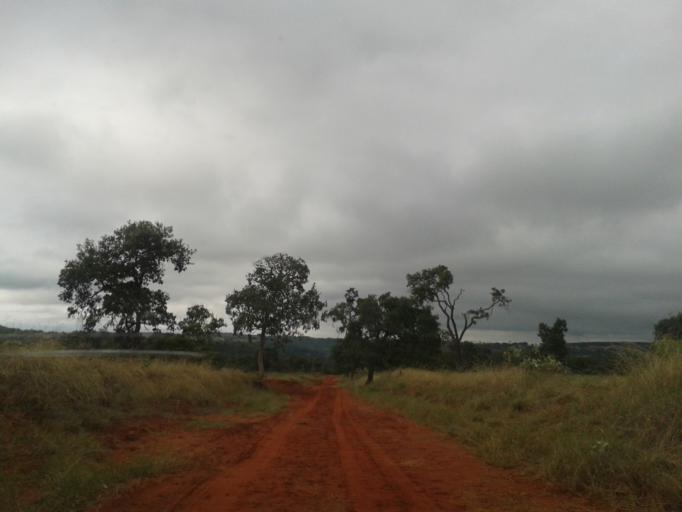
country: BR
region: Minas Gerais
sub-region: Campina Verde
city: Campina Verde
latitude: -19.4179
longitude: -49.6329
